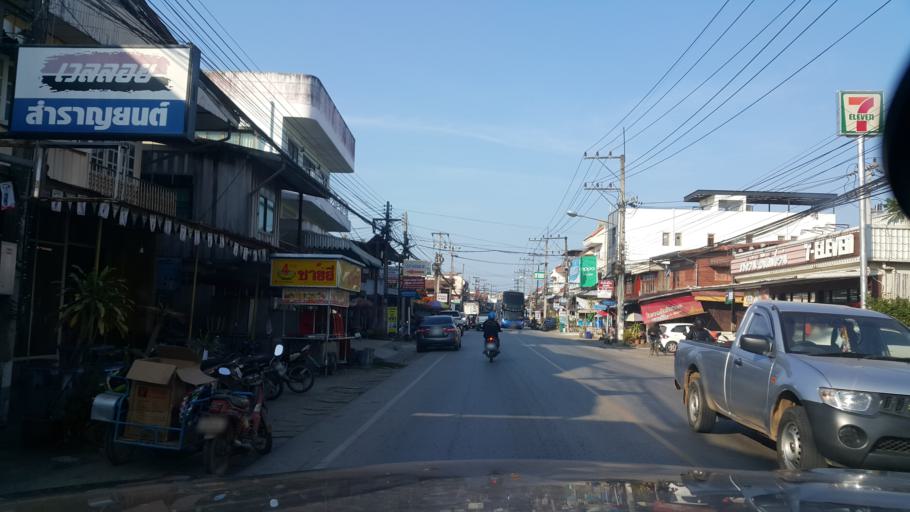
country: TH
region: Loei
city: Chiang Khan
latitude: 17.8937
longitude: 101.6548
